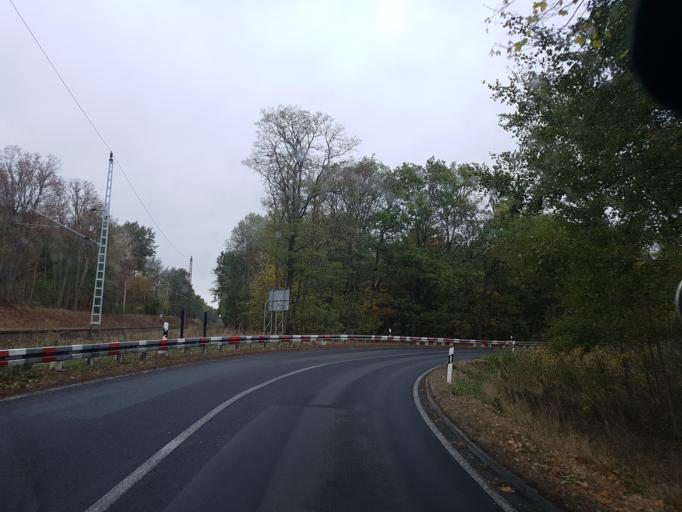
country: DE
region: Brandenburg
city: Falkenberg
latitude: 51.6053
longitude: 13.2376
